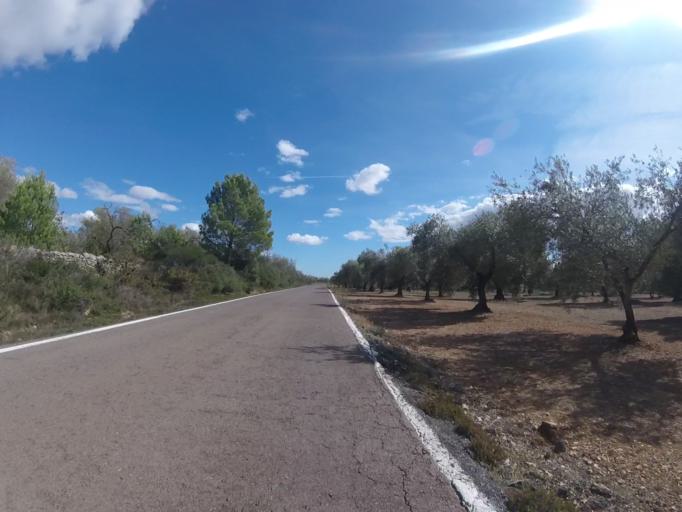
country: ES
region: Valencia
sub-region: Provincia de Castello
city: Albocasser
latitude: 40.4026
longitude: 0.0825
